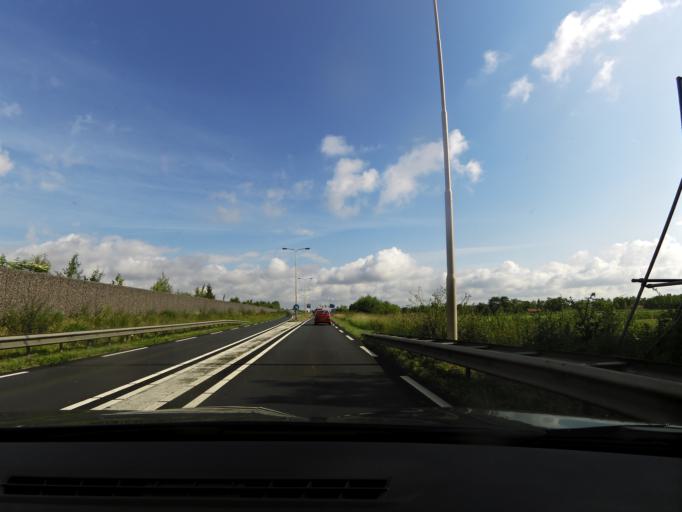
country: NL
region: Utrecht
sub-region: Gemeente Veenendaal
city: Veenendaal
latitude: 52.0322
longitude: 5.5804
